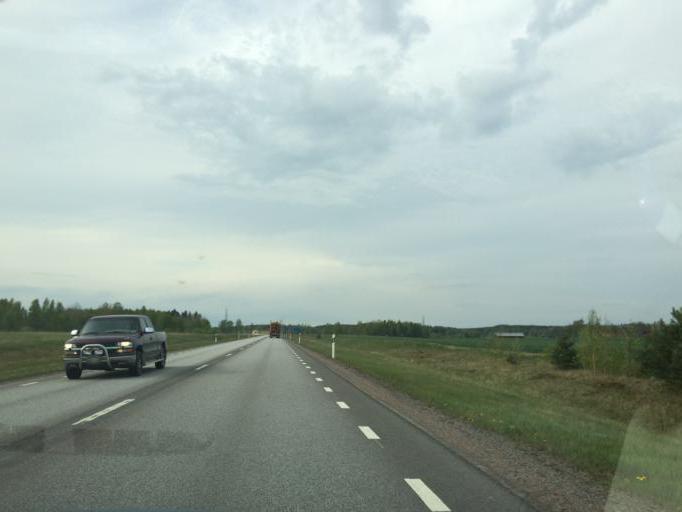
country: SE
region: Vaestmanland
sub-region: Kopings Kommun
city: Koping
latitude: 59.5311
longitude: 15.9575
